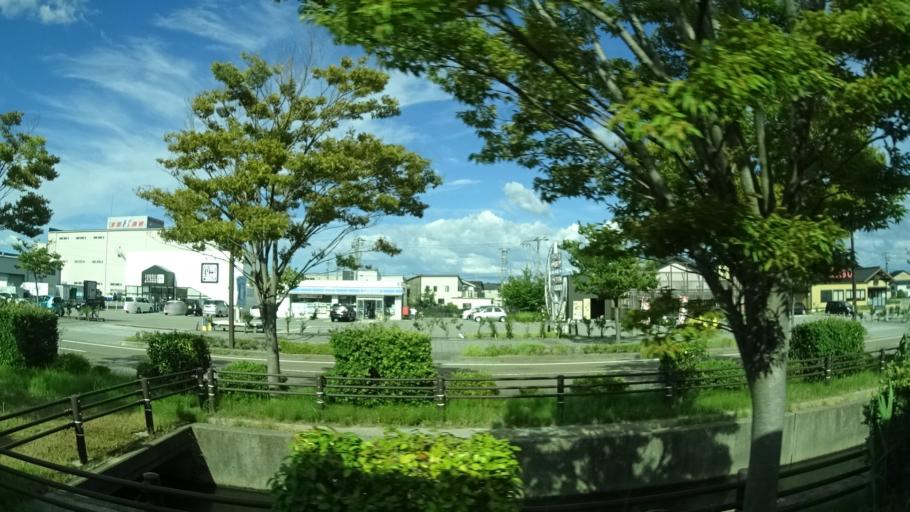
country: JP
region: Ishikawa
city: Kanazawa-shi
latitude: 36.6044
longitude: 136.6190
